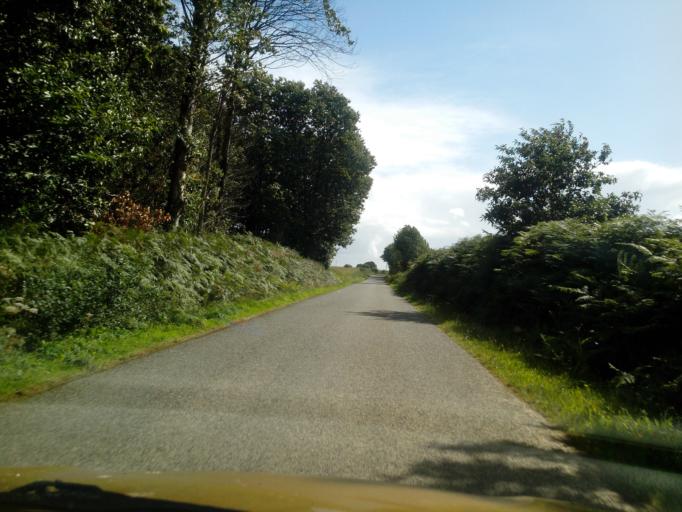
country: FR
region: Brittany
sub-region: Departement des Cotes-d'Armor
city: Merdrignac
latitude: 48.1675
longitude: -2.4188
